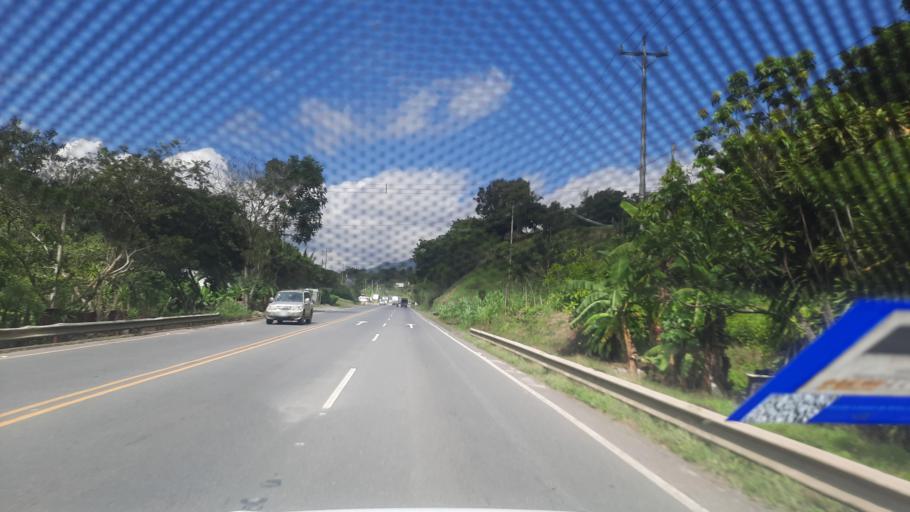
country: CR
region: Alajuela
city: Esquipulas
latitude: 10.0794
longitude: -84.4321
